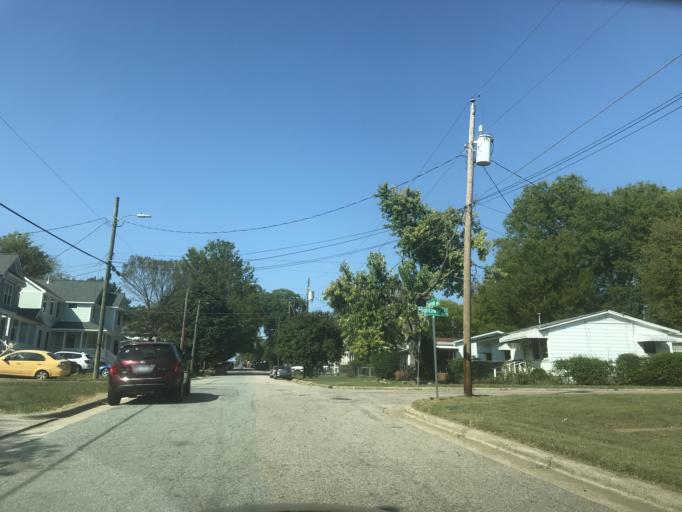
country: US
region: North Carolina
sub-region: Wake County
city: Raleigh
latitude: 35.7695
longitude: -78.6225
